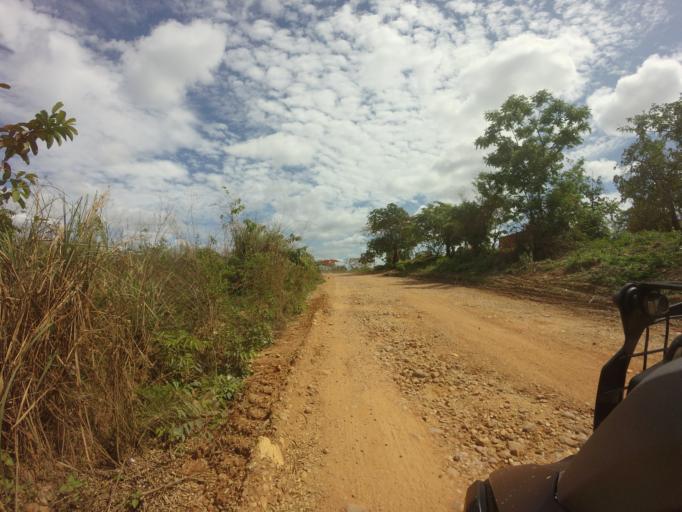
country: CD
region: Bas-Congo
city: Matadi
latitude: -6.0460
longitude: 13.5925
